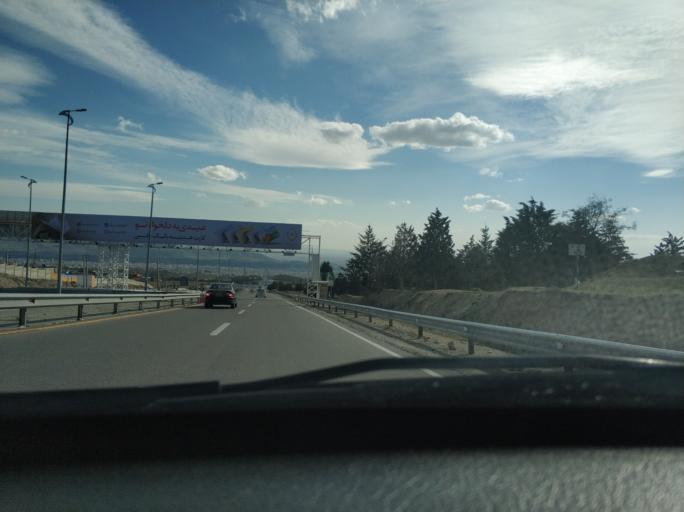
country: IR
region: Tehran
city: Tajrish
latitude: 35.7856
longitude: 51.5655
